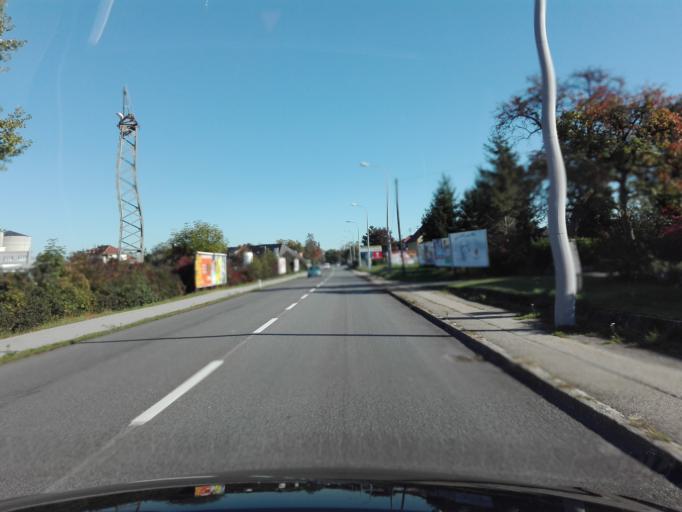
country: AT
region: Upper Austria
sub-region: Politischer Bezirk Linz-Land
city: Enns
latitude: 48.2166
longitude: 14.4510
